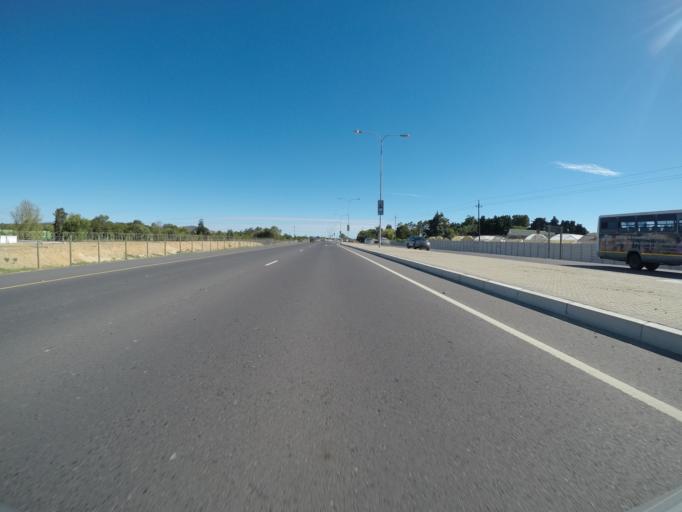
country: ZA
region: Western Cape
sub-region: Cape Winelands District Municipality
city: Stellenbosch
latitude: -33.9926
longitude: 18.7648
